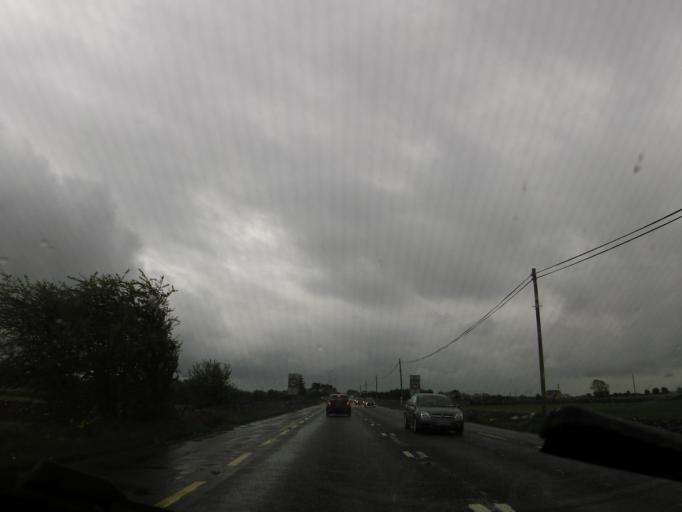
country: IE
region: Connaught
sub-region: County Galway
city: Claregalway
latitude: 53.3941
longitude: -8.9134
